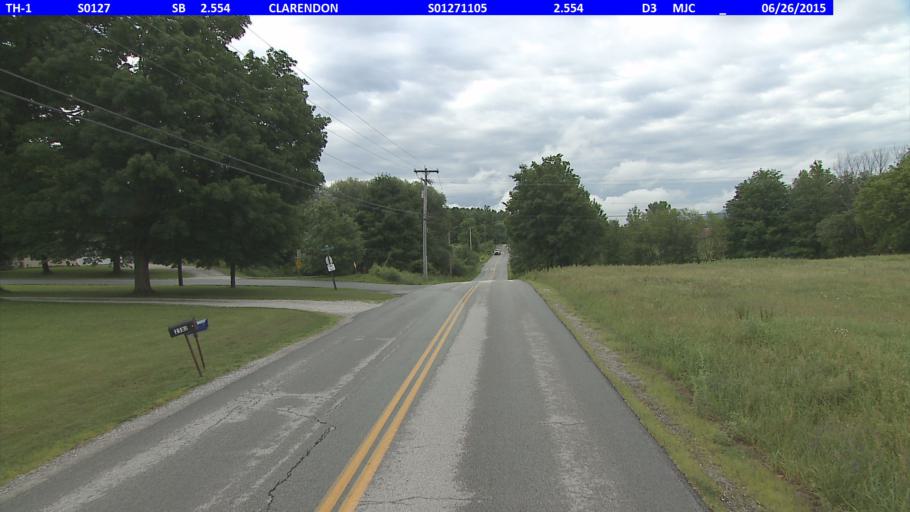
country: US
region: Vermont
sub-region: Rutland County
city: Rutland
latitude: 43.5510
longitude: -72.9704
